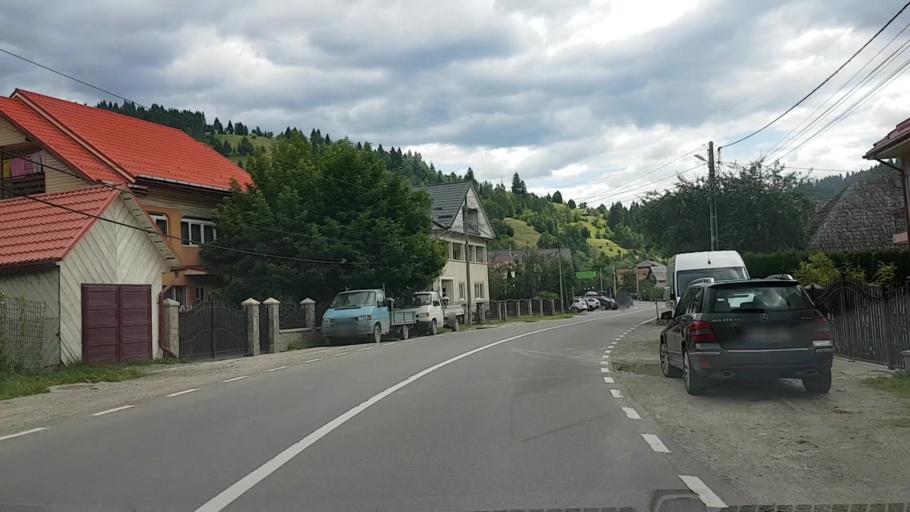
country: RO
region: Neamt
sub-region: Comuna Farcasa
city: Farcasa
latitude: 47.1573
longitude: 25.8364
